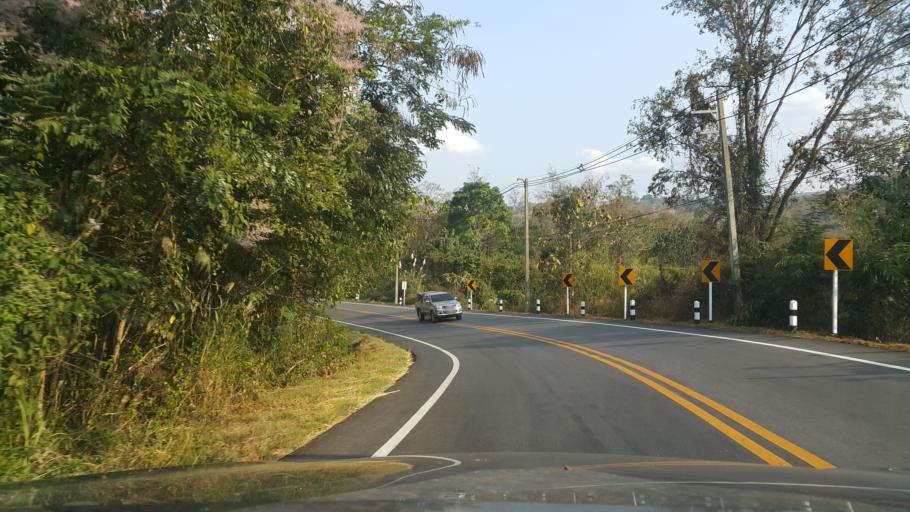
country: TH
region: Loei
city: Dan Sai
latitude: 17.2309
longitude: 101.0933
